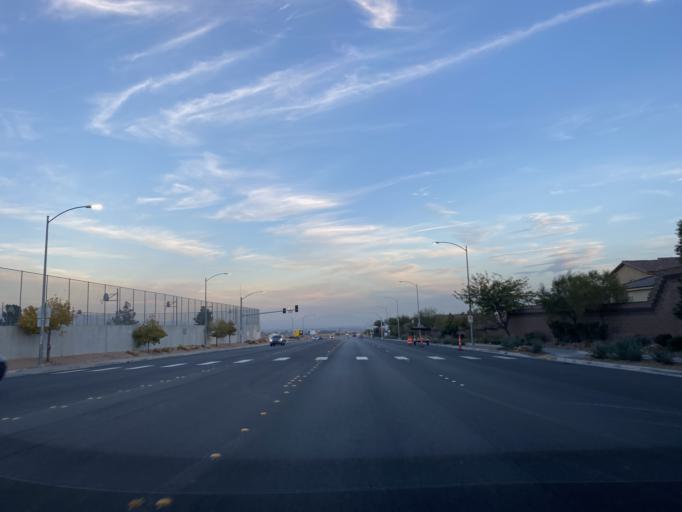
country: US
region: Nevada
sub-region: Clark County
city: Summerlin South
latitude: 36.2773
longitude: -115.3177
